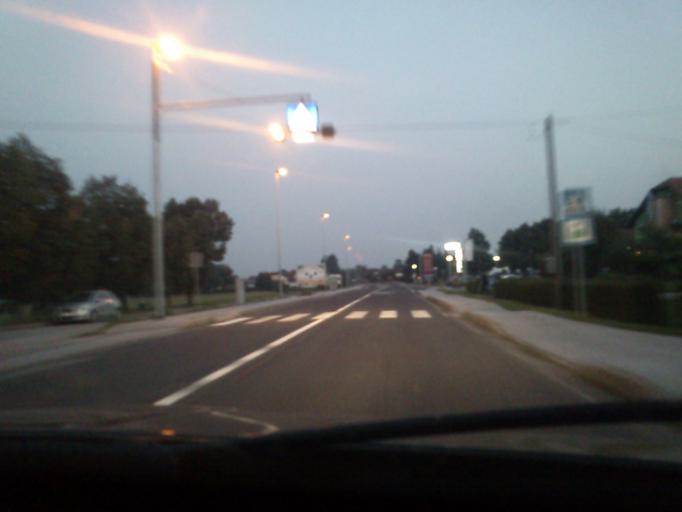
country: SI
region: Hajdina
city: Spodnja Hajdina
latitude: 46.4272
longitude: 15.8270
